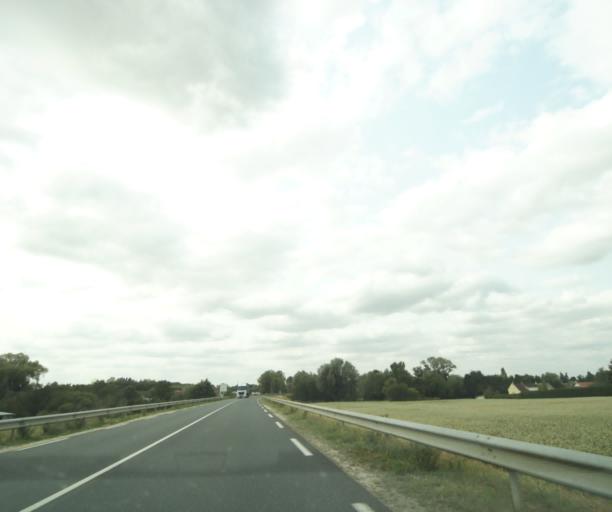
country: FR
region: Centre
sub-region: Departement de l'Indre
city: Buzancais
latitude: 46.8818
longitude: 1.4110
